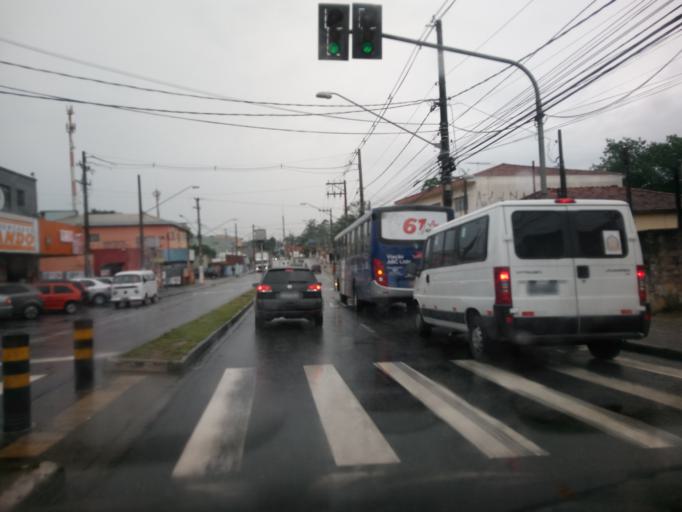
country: BR
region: Sao Paulo
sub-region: Sao Bernardo Do Campo
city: Sao Bernardo do Campo
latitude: -23.7552
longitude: -46.5767
